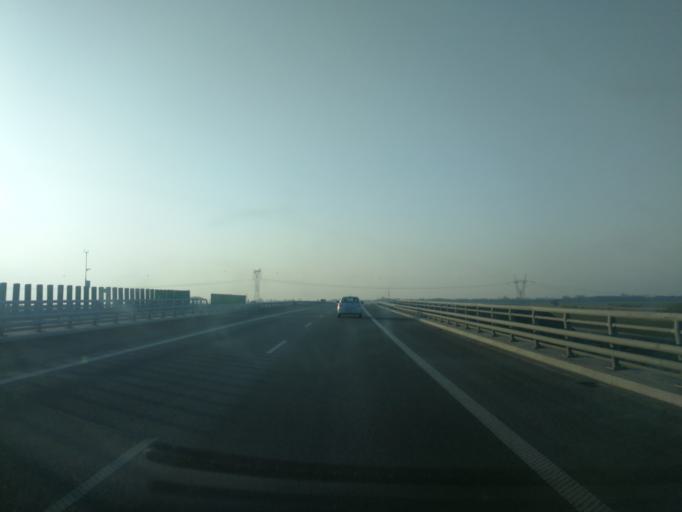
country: PL
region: Warmian-Masurian Voivodeship
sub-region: Powiat elblaski
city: Gronowo Elblaskie
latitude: 54.1663
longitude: 19.2394
